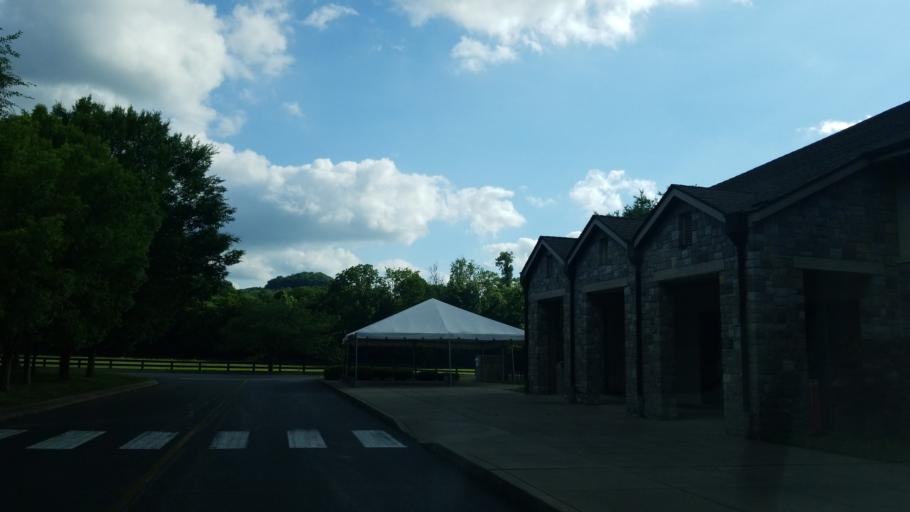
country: US
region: Tennessee
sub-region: Davidson County
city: Forest Hills
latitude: 36.0306
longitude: -86.8577
